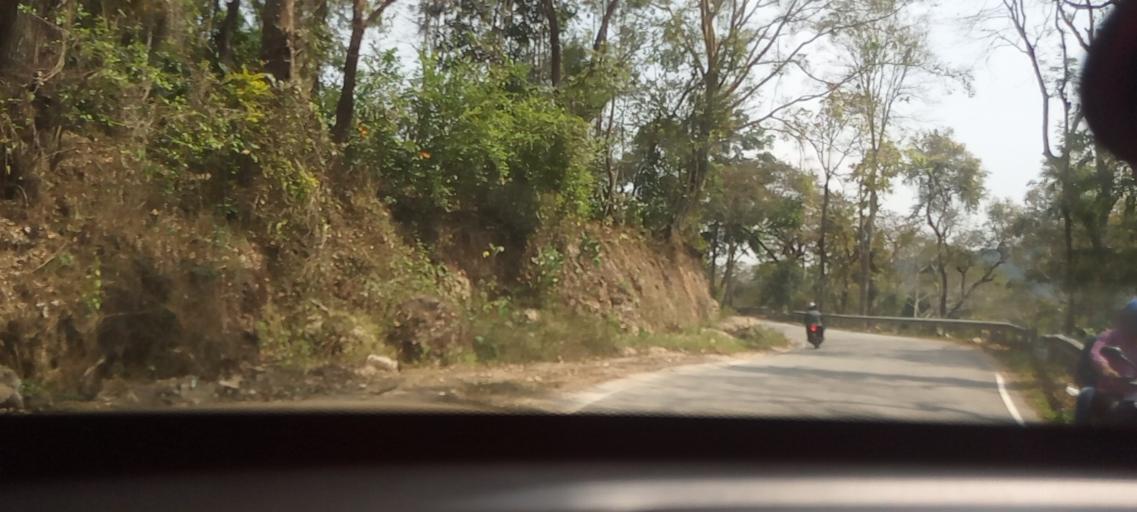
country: IN
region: Karnataka
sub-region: Chikmagalur
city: Mudigere
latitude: 13.2743
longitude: 75.6102
